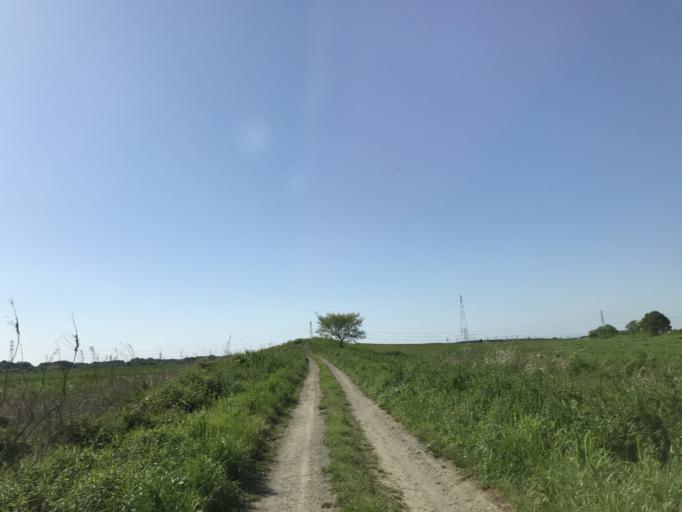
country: JP
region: Ibaraki
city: Moriya
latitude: 35.9398
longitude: 139.9466
